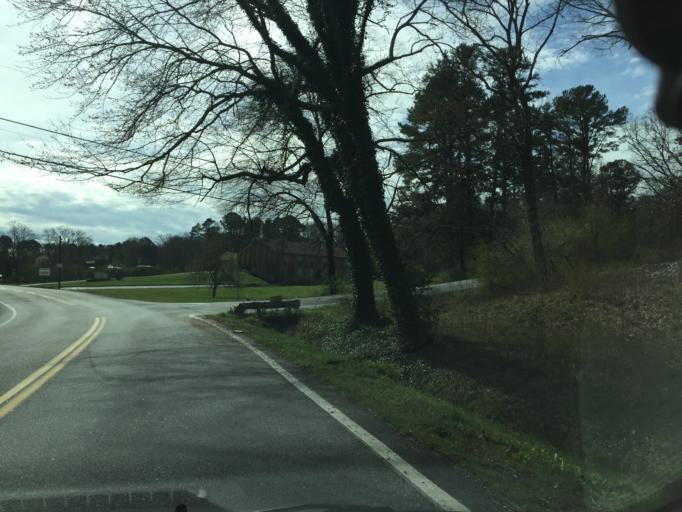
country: US
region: Tennessee
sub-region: Hamilton County
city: East Brainerd
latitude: 35.0347
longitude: -85.1082
